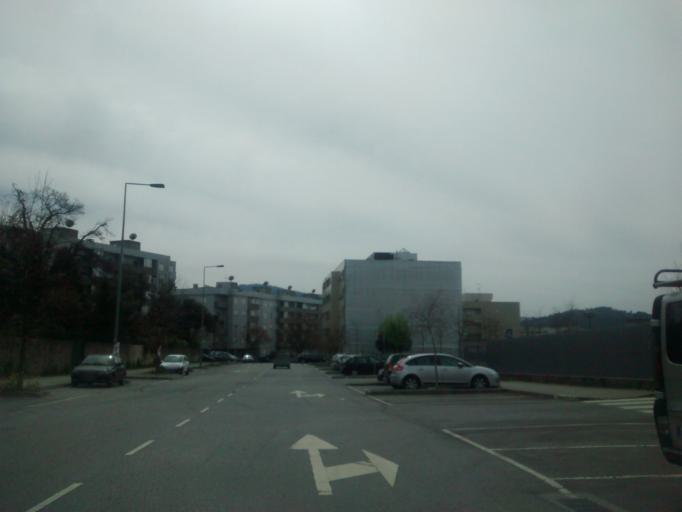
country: PT
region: Braga
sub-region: Braga
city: Braga
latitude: 41.5584
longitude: -8.4038
